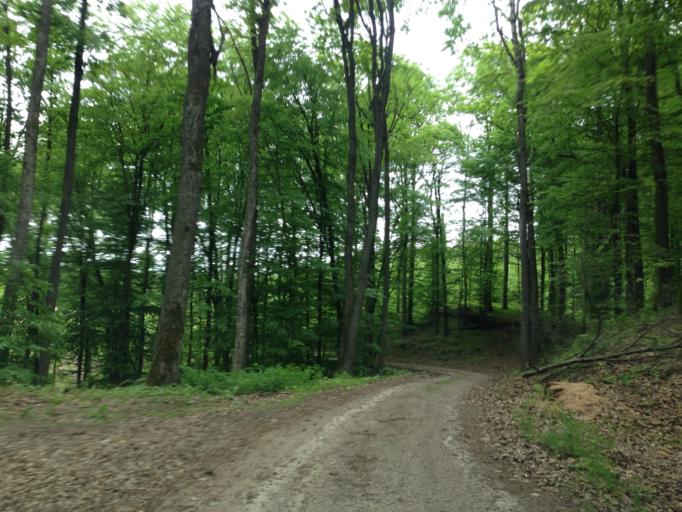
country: PL
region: Kujawsko-Pomorskie
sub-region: Powiat brodnicki
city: Gorzno
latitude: 53.2627
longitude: 19.7105
